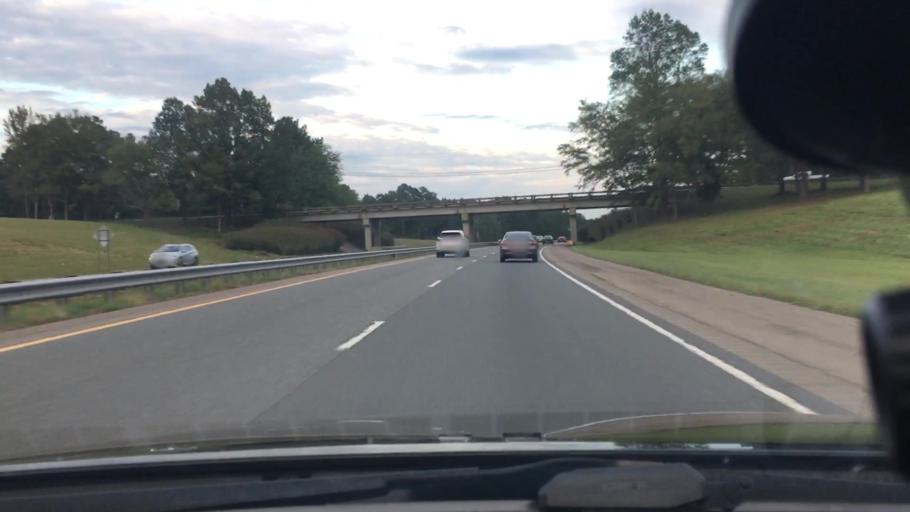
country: US
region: North Carolina
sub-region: Chatham County
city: Pittsboro
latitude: 35.6238
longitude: -79.0891
